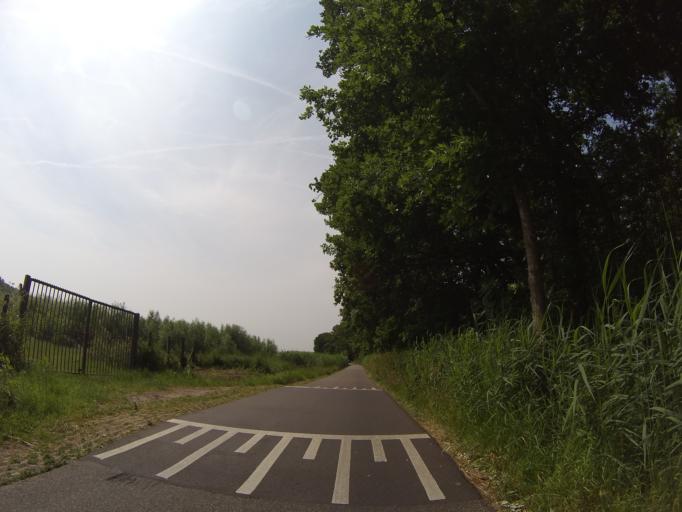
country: NL
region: Utrecht
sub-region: Gemeente Bunnik
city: Bunnik
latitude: 52.0871
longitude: 5.1982
